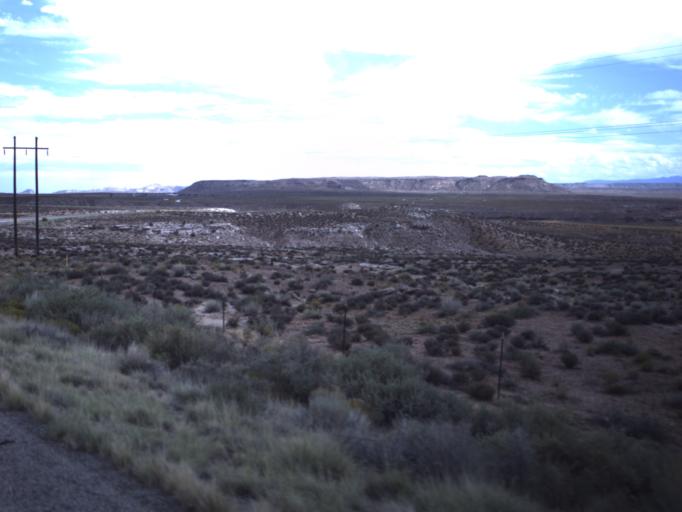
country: US
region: Utah
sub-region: San Juan County
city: Blanding
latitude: 37.2799
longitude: -109.3659
